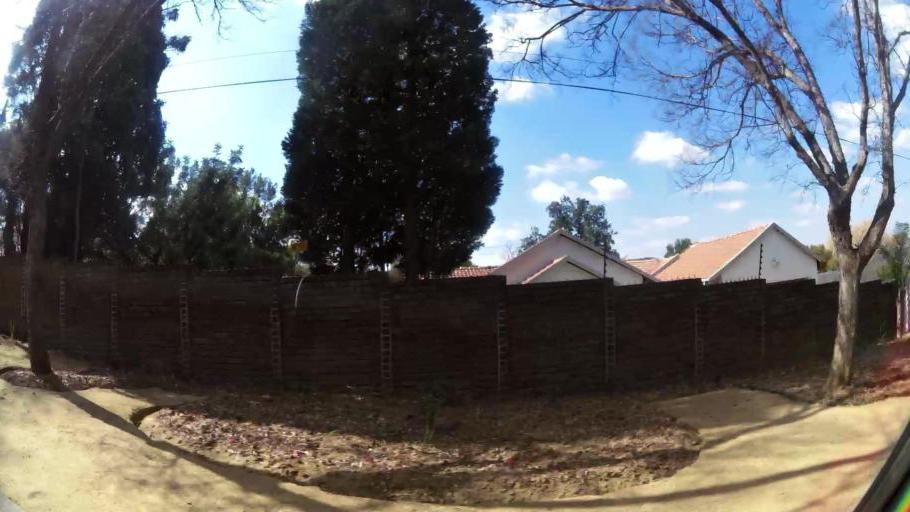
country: ZA
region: Gauteng
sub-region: West Rand District Municipality
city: Muldersdriseloop
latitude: -26.0608
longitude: 27.9680
